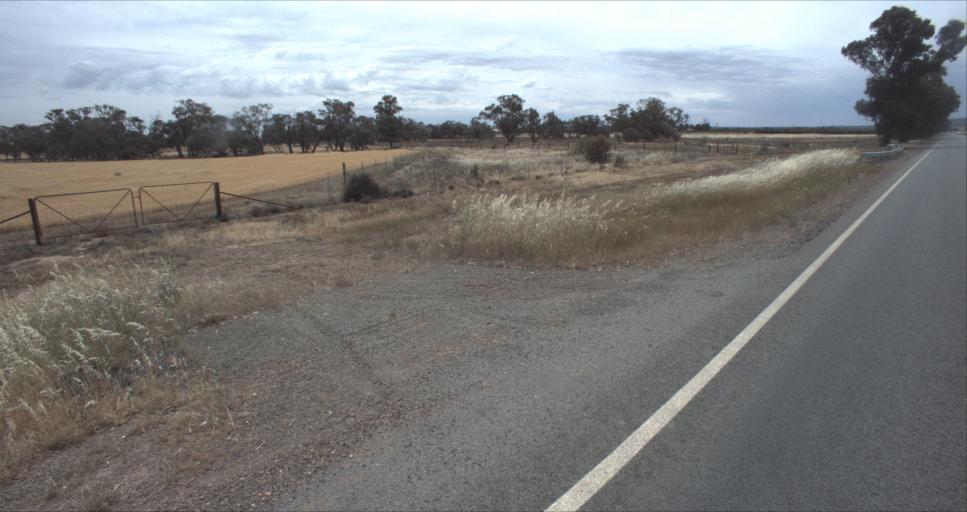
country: AU
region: New South Wales
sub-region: Leeton
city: Leeton
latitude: -34.5156
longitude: 146.4174
